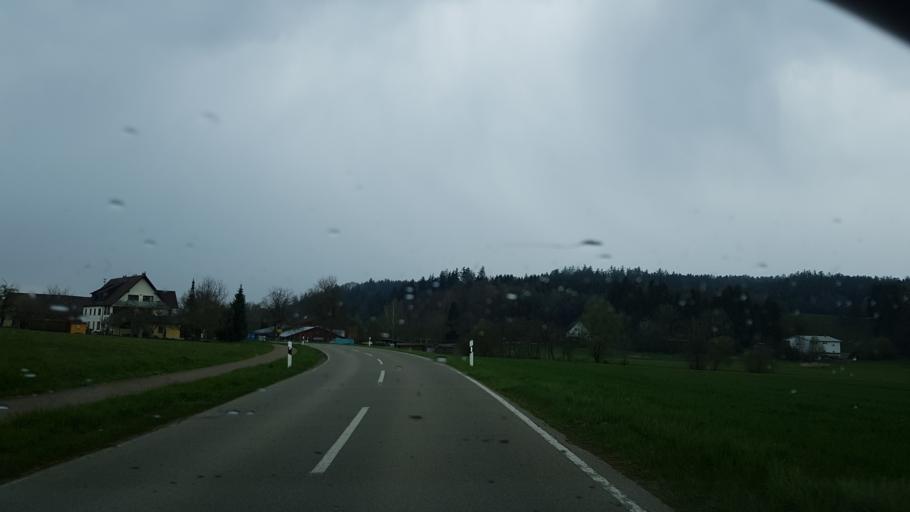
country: DE
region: Baden-Wuerttemberg
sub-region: Tuebingen Region
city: Wain
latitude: 48.2276
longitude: 10.0202
